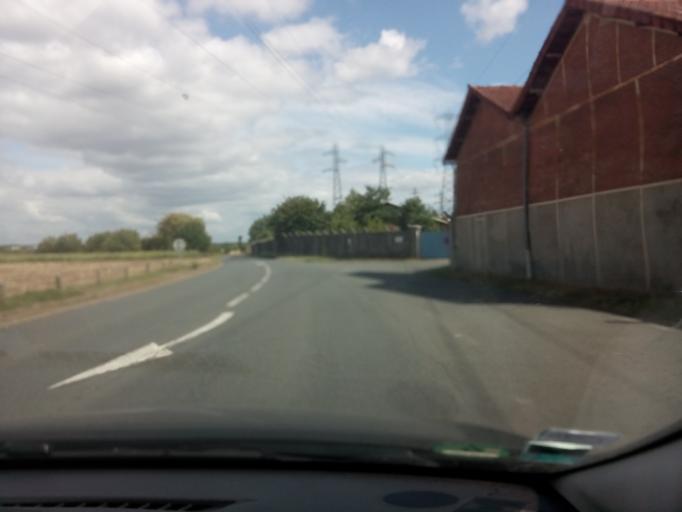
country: FR
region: Ile-de-France
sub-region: Departement des Yvelines
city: Jouy-en-Josas
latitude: 48.7498
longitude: 2.1679
